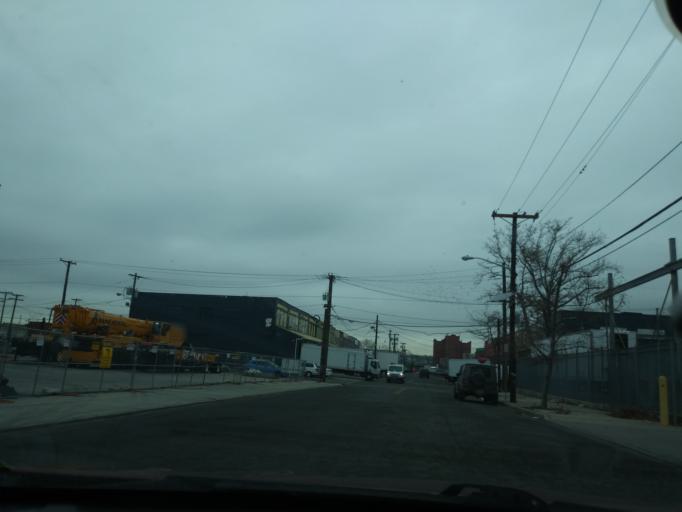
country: US
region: New Jersey
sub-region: Essex County
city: Newark
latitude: 40.7173
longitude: -74.1759
